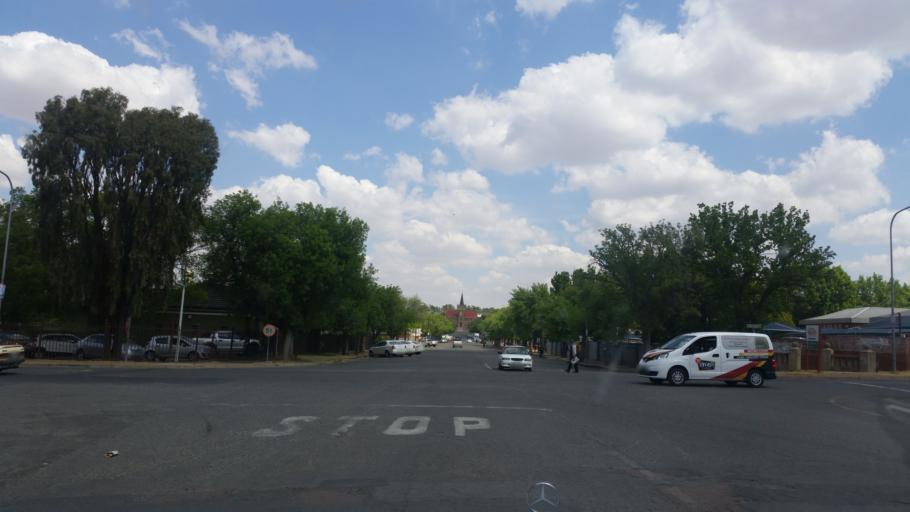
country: ZA
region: Orange Free State
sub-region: Thabo Mofutsanyana District Municipality
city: Reitz
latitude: -27.7988
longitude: 28.4312
